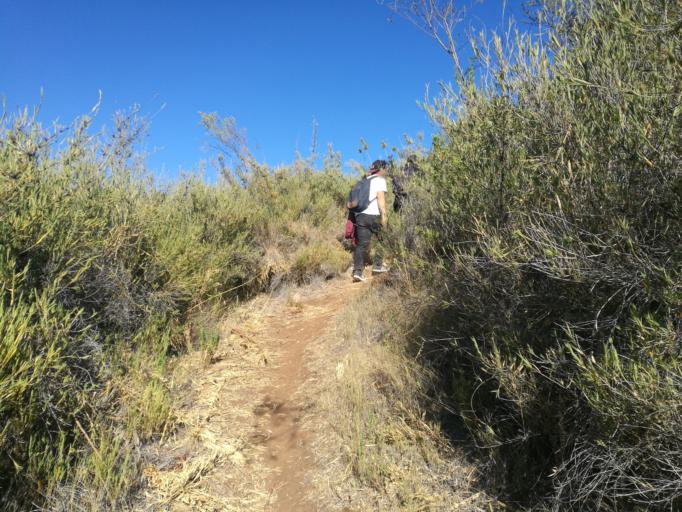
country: CL
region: Valparaiso
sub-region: Provincia de Valparaiso
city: Valparaiso
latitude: -33.0780
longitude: -71.6450
